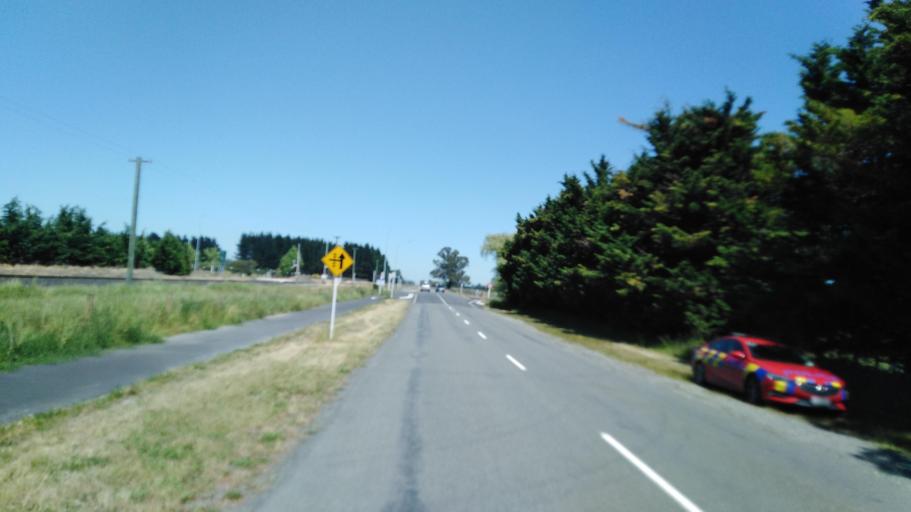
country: NZ
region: Canterbury
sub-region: Selwyn District
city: Prebbleton
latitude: -43.5598
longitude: 172.4592
